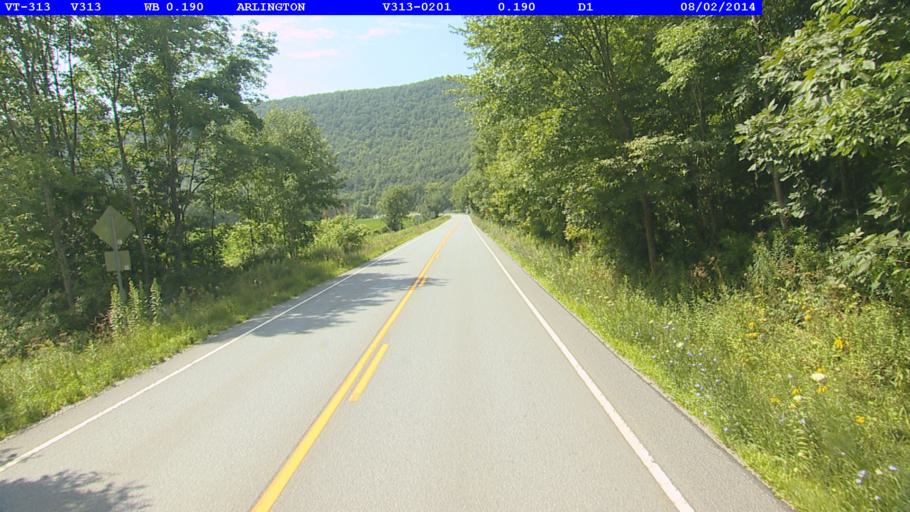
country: US
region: Vermont
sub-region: Bennington County
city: Arlington
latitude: 43.1072
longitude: -73.2614
